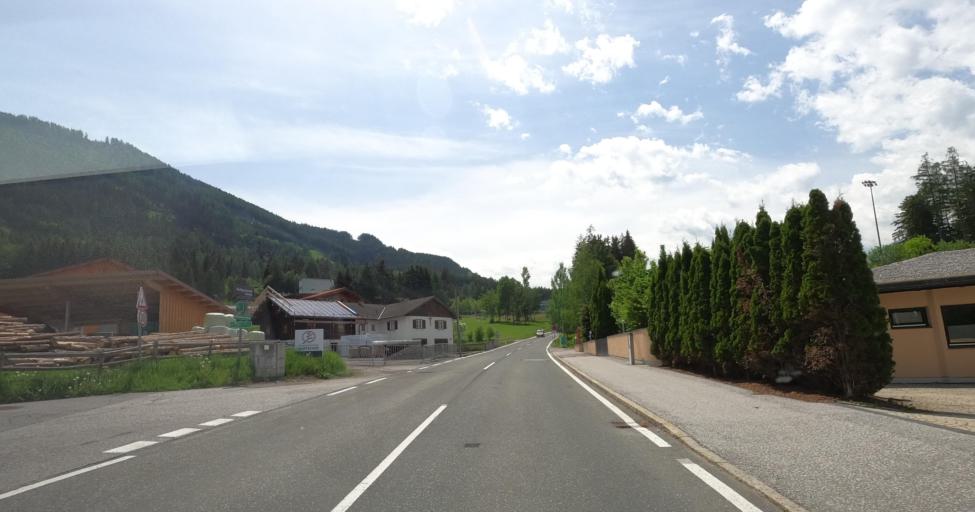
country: AT
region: Tyrol
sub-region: Politischer Bezirk Innsbruck Land
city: Sistrans
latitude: 47.2251
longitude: 11.4295
